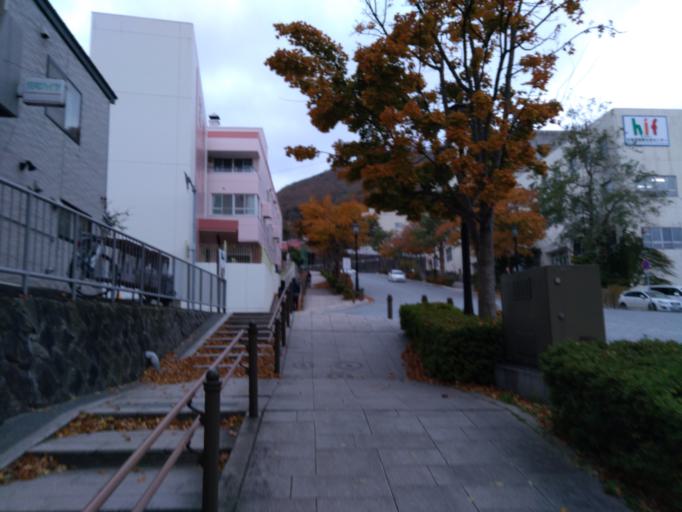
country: JP
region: Hokkaido
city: Hakodate
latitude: 41.7645
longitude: 140.7126
